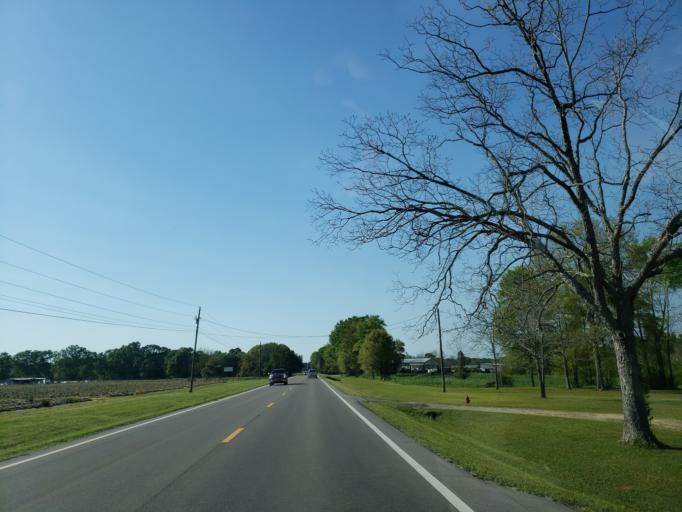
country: US
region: Mississippi
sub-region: Perry County
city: Richton
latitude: 31.3983
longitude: -88.9432
